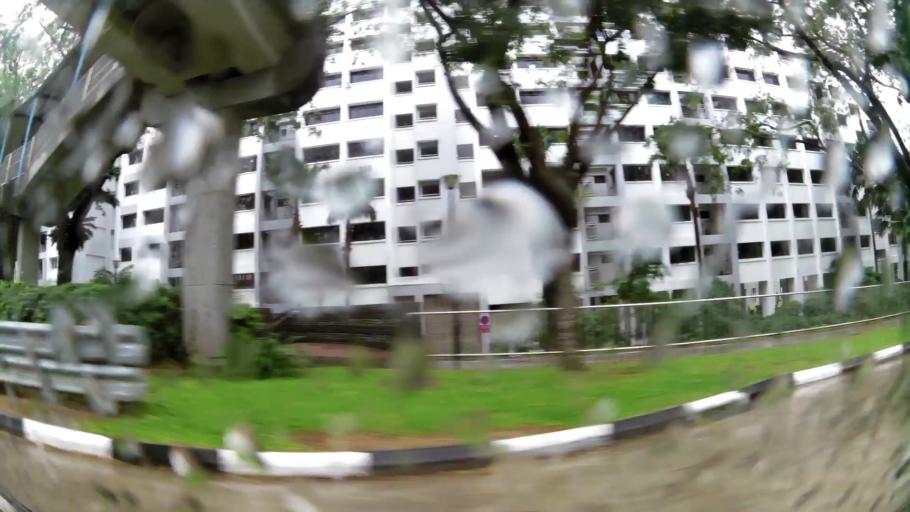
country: MY
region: Johor
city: Kampung Pasir Gudang Baru
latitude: 1.3912
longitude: 103.8997
